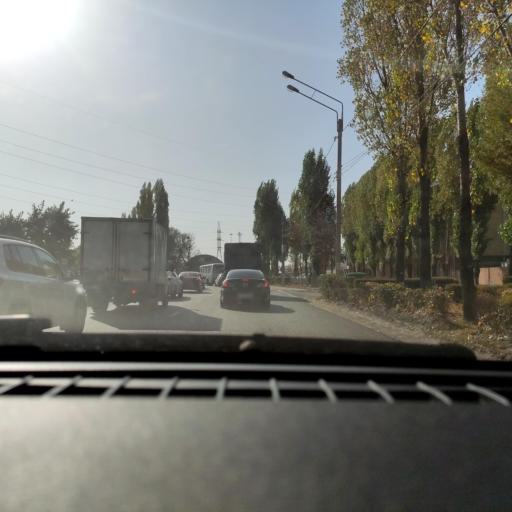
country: RU
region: Voronezj
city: Voronezh
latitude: 51.6483
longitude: 39.2678
